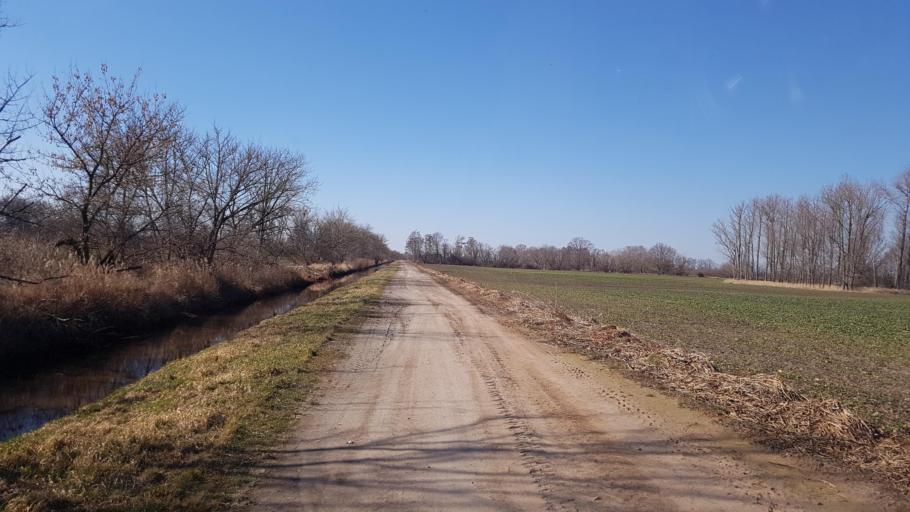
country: DE
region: Brandenburg
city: Grossthiemig
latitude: 51.4119
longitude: 13.6608
